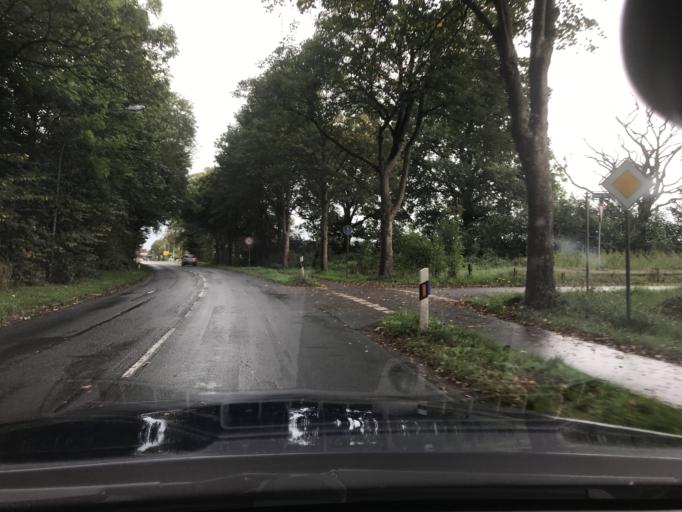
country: DE
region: Lower Saxony
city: Stade
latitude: 53.5790
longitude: 9.4714
